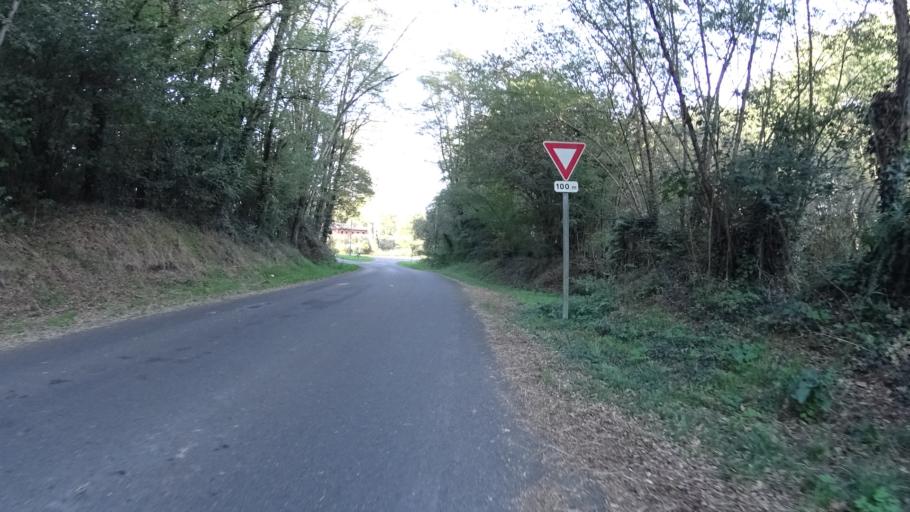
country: FR
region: Aquitaine
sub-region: Departement des Landes
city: Saint-Paul-les-Dax
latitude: 43.7374
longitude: -1.0436
